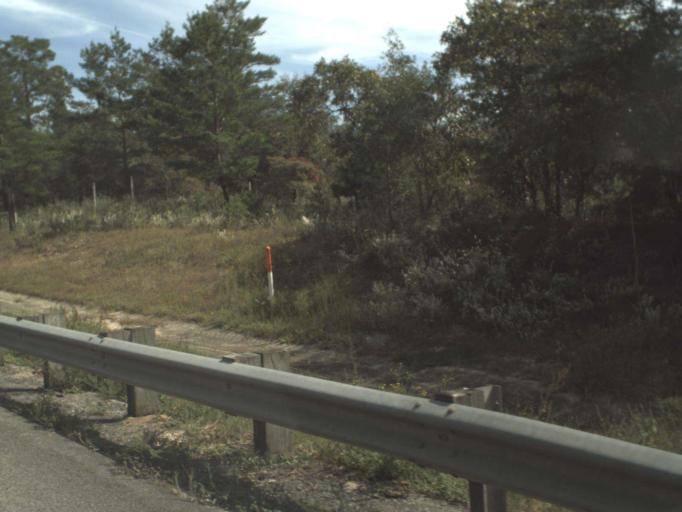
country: US
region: Florida
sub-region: Bay County
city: Lynn Haven
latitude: 30.4498
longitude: -85.6872
